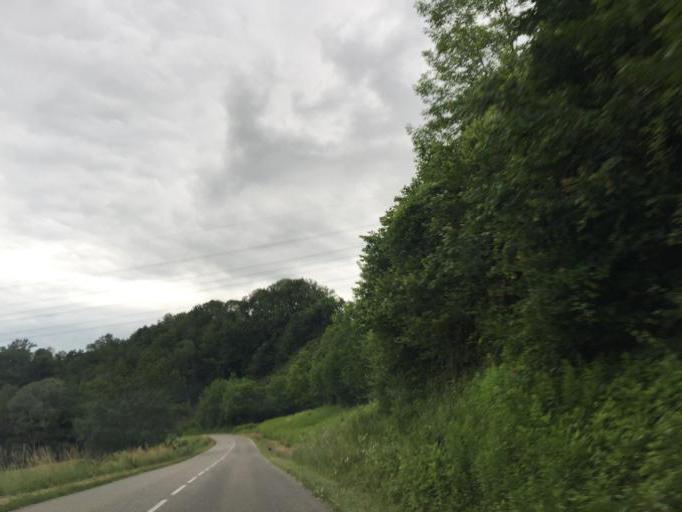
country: FR
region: Rhone-Alpes
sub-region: Departement de la Savoie
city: Le Pont-de-Beauvoisin
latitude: 45.5433
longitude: 5.6815
